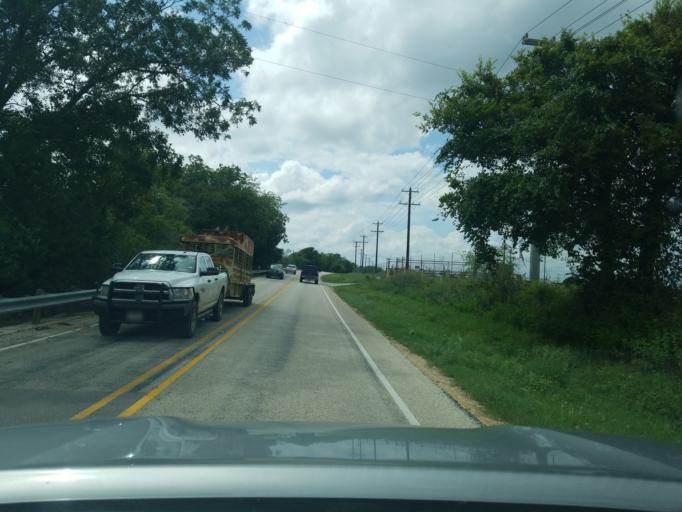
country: US
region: Texas
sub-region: Blanco County
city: Blanco
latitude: 30.0916
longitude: -98.3803
